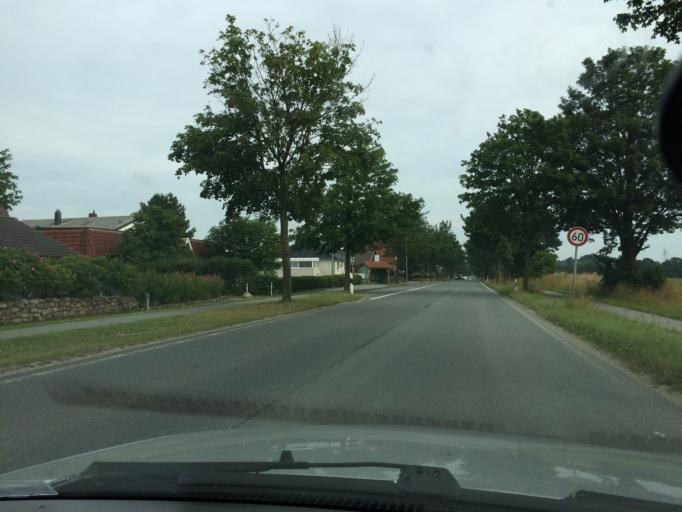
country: DE
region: Schleswig-Holstein
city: Jarplund-Weding
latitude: 54.7409
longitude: 9.4402
